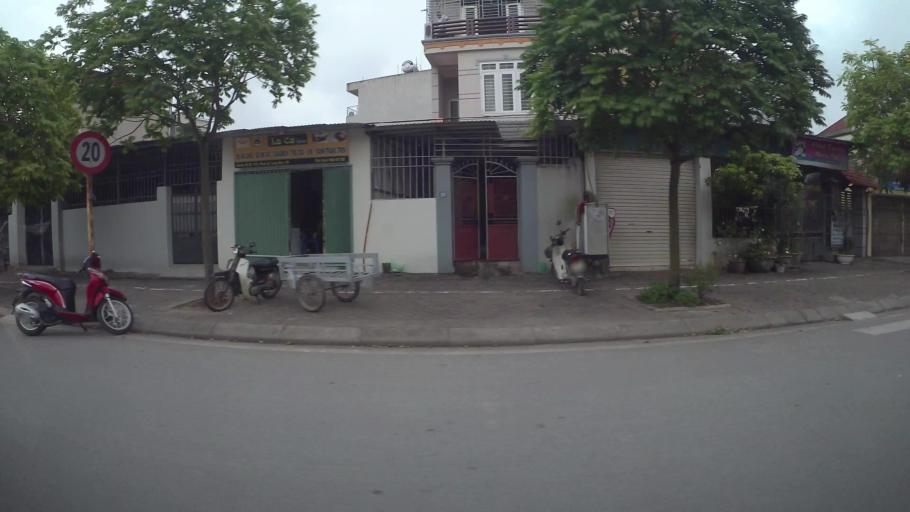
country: VN
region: Ha Noi
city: Trau Quy
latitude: 21.0477
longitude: 105.9245
